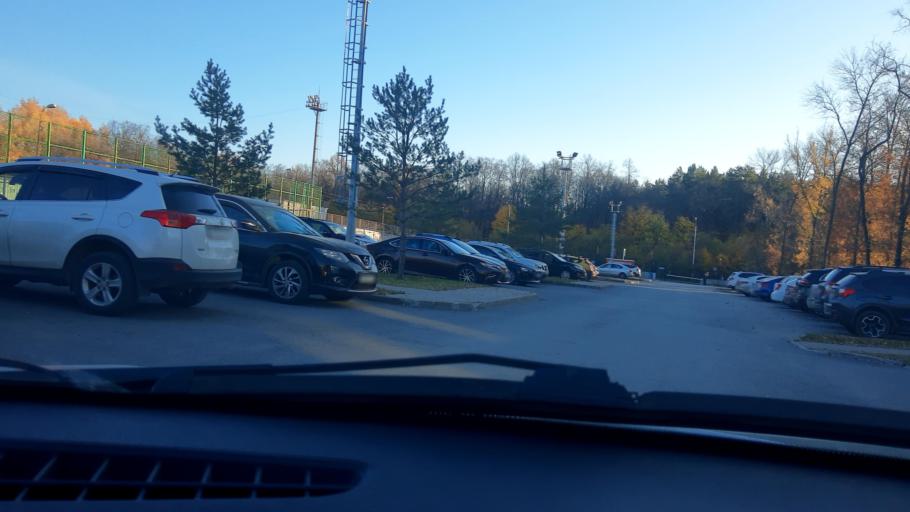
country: RU
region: Bashkortostan
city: Ufa
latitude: 54.7389
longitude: 56.0224
